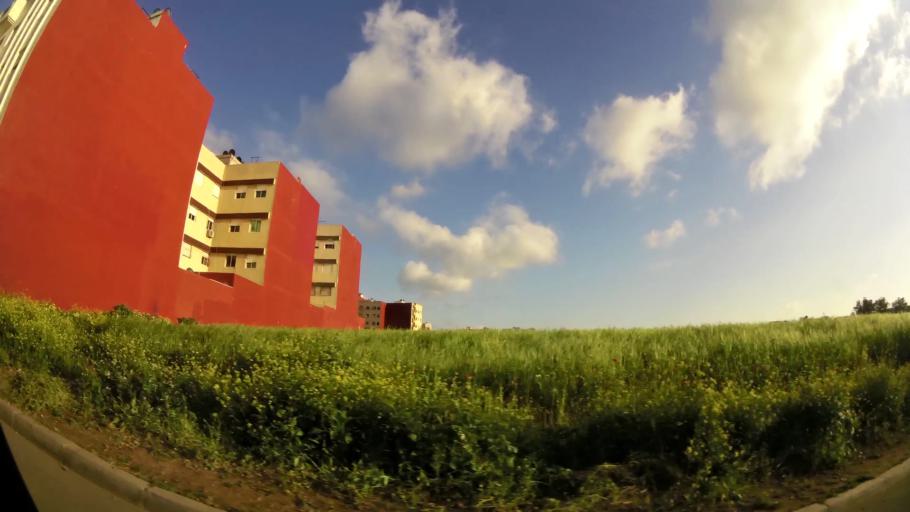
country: MA
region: Chaouia-Ouardigha
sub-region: Settat Province
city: Settat
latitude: 33.0014
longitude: -7.6016
